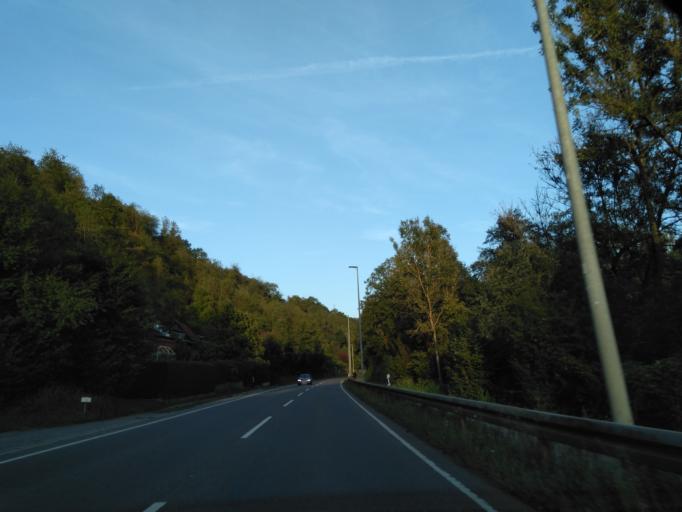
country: DE
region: Baden-Wuerttemberg
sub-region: Regierungsbezirk Stuttgart
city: Bietigheim-Bissingen
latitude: 48.9494
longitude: 9.0938
